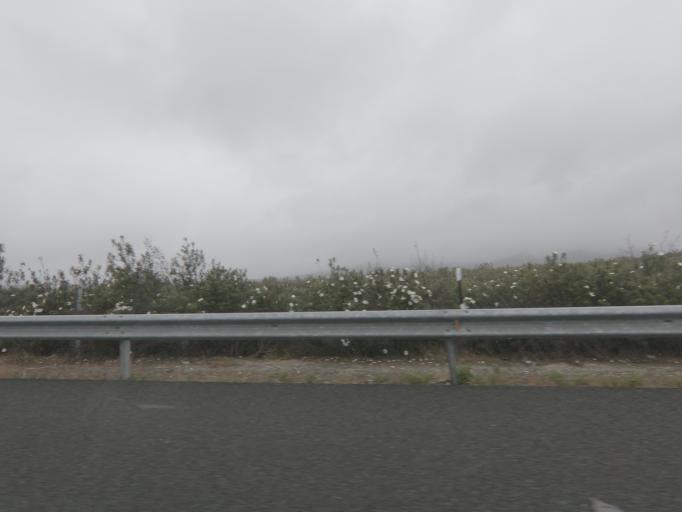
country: ES
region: Extremadura
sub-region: Provincia de Caceres
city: Canaveral
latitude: 39.7771
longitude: -6.3868
